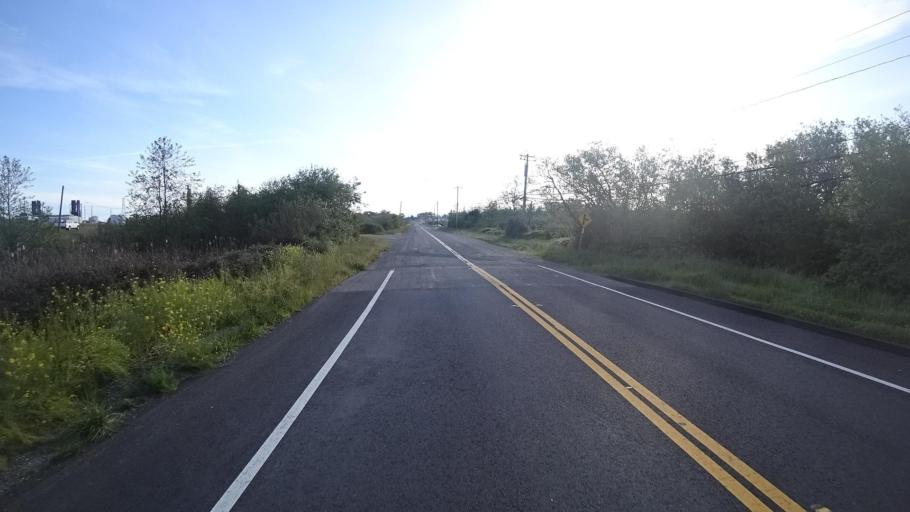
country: US
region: California
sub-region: Humboldt County
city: Humboldt Hill
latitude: 40.7364
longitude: -124.2090
